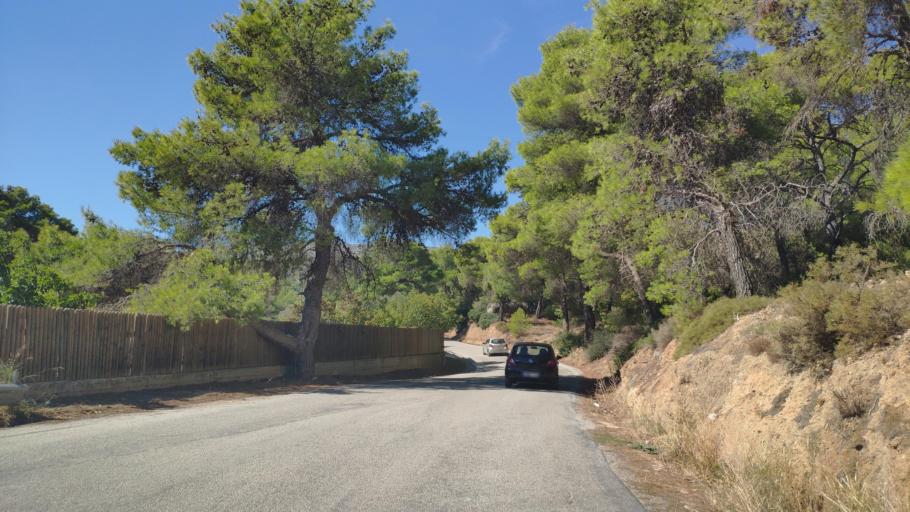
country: GR
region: Attica
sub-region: Nomarchia Anatolikis Attikis
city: Kouvaras
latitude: 37.8395
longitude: 24.0060
